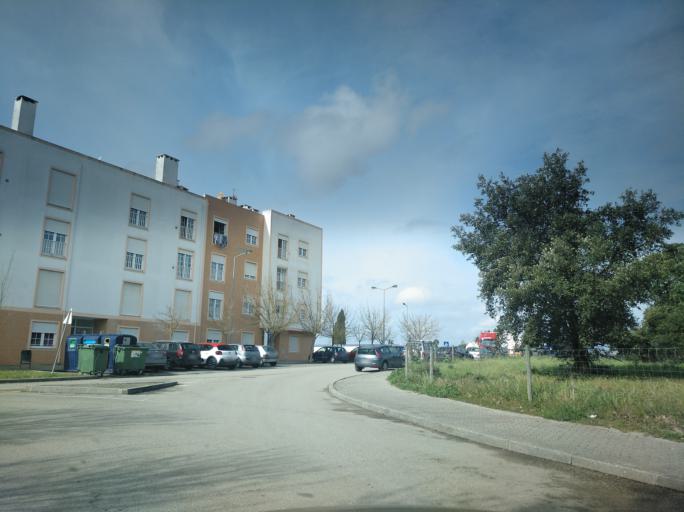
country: PT
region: Setubal
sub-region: Grandola
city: Grandola
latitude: 38.1739
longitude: -8.5601
